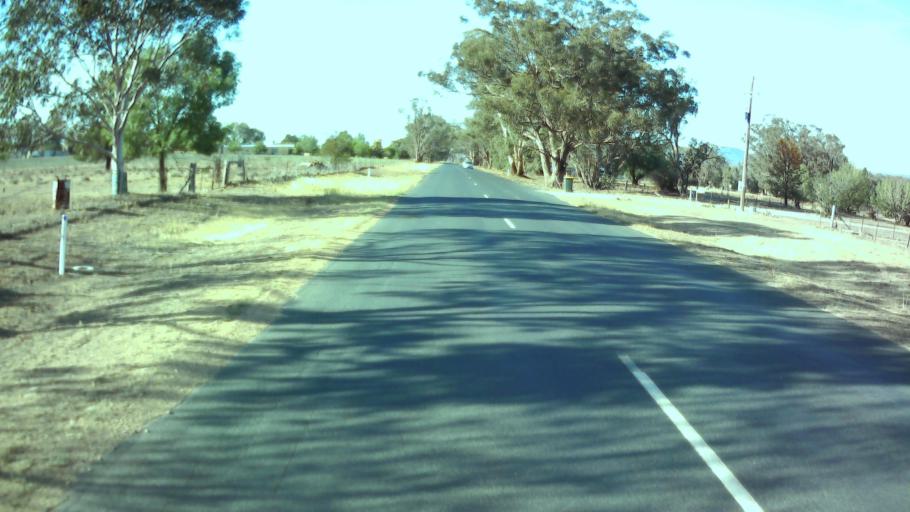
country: AU
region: New South Wales
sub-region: Weddin
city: Grenfell
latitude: -33.9117
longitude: 148.1443
